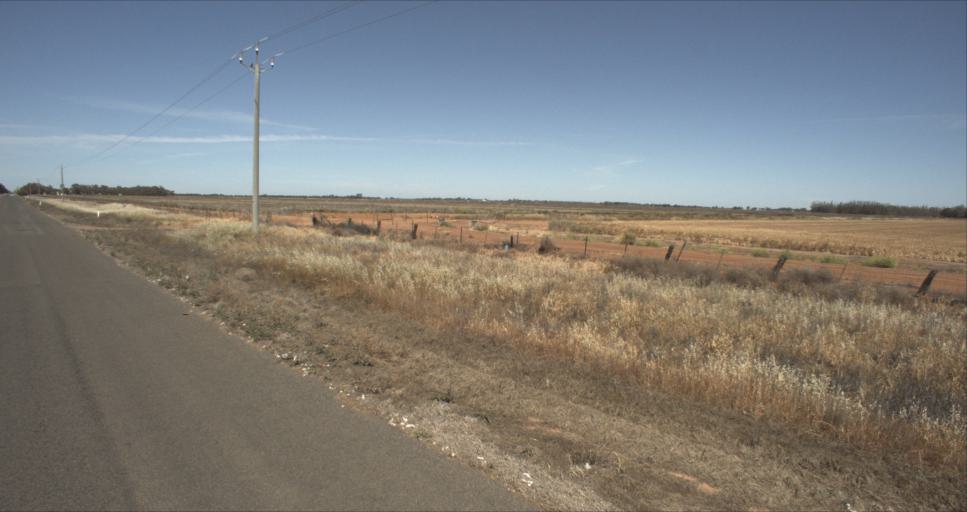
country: AU
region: New South Wales
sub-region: Leeton
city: Leeton
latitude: -34.4867
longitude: 146.2895
